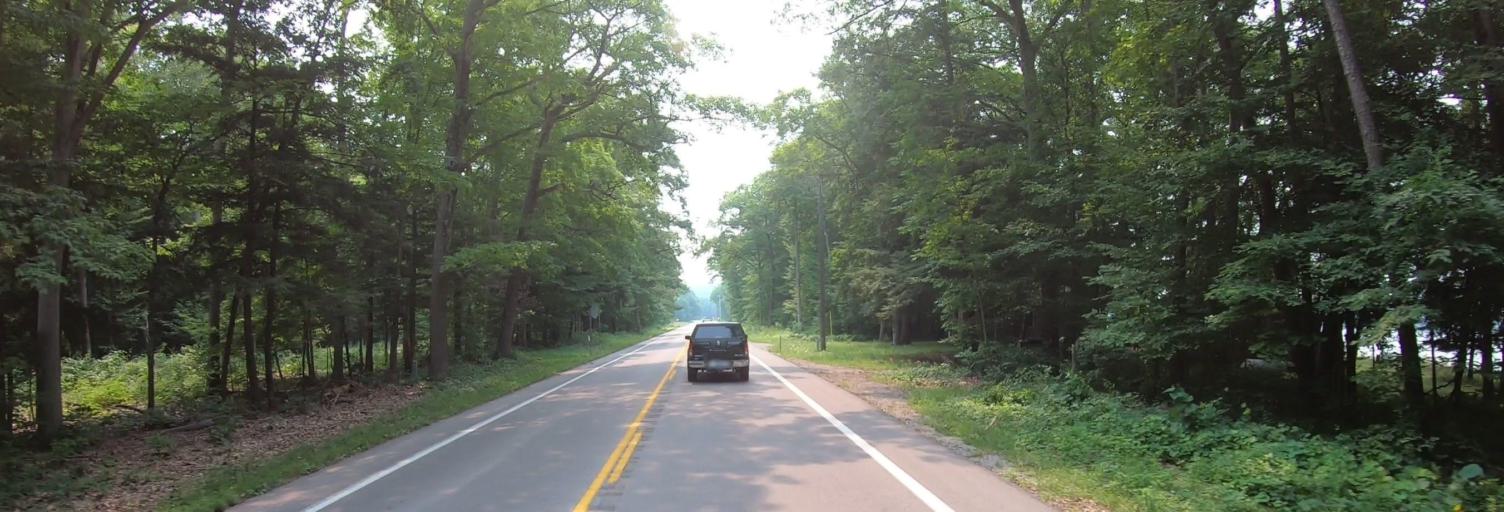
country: US
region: Michigan
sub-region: Leelanau County
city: Leland
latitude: 44.9280
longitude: -85.8835
